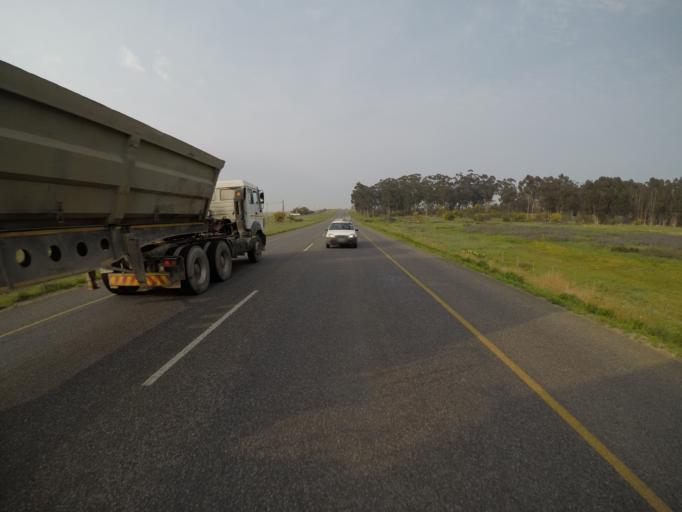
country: ZA
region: Western Cape
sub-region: West Coast District Municipality
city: Malmesbury
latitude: -33.6131
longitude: 18.7273
